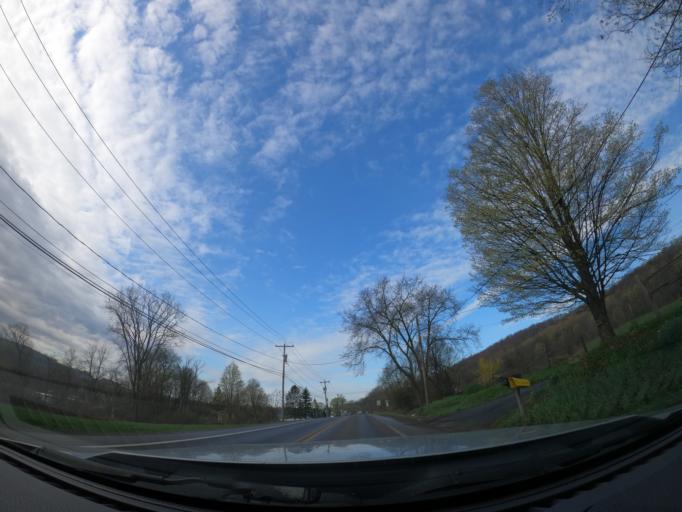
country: US
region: New York
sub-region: Cortland County
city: Homer
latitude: 42.6304
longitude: -76.1491
